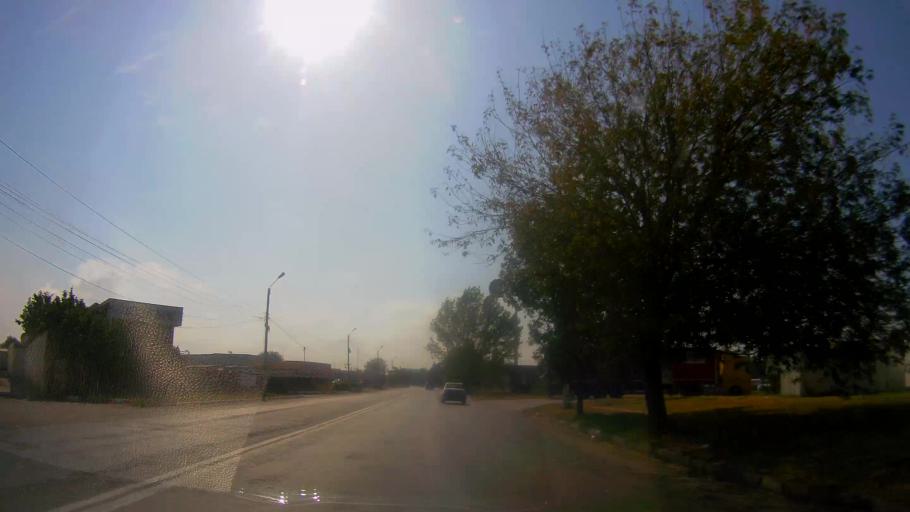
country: RO
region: Giurgiu
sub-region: Comuna Fratesti
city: Remus
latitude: 43.9143
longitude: 25.9726
